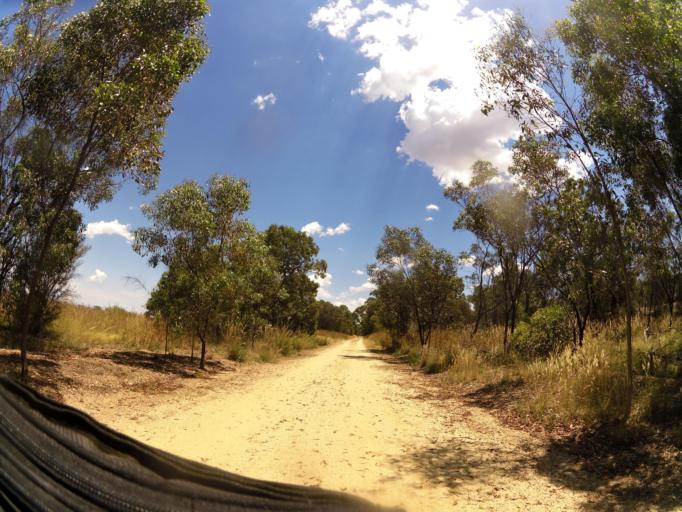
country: AU
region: Victoria
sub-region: Wellington
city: Heyfield
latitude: -37.9790
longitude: 146.8491
